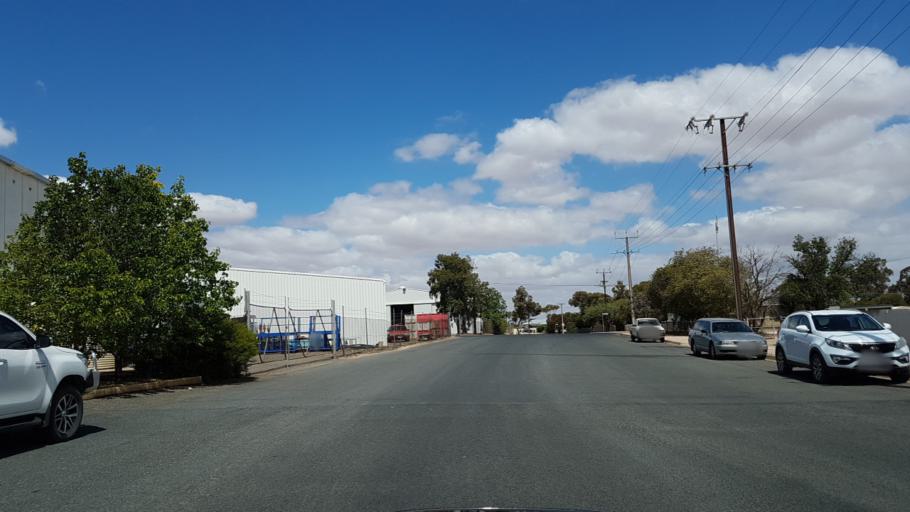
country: AU
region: South Australia
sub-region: Loxton Waikerie
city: Waikerie
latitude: -34.1823
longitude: 139.9892
